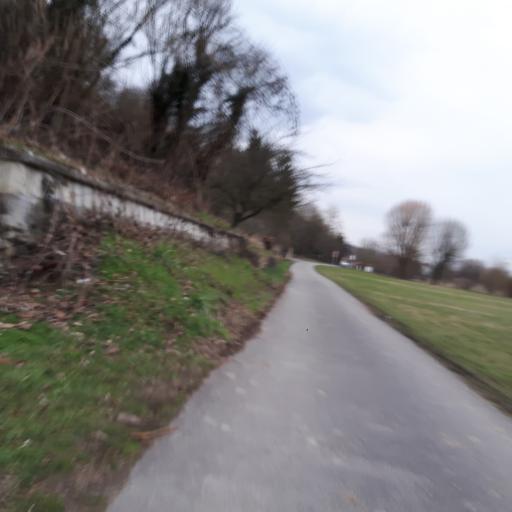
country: DE
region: Baden-Wuerttemberg
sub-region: Regierungsbezirk Stuttgart
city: Pleidelsheim
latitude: 48.9576
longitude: 9.1850
